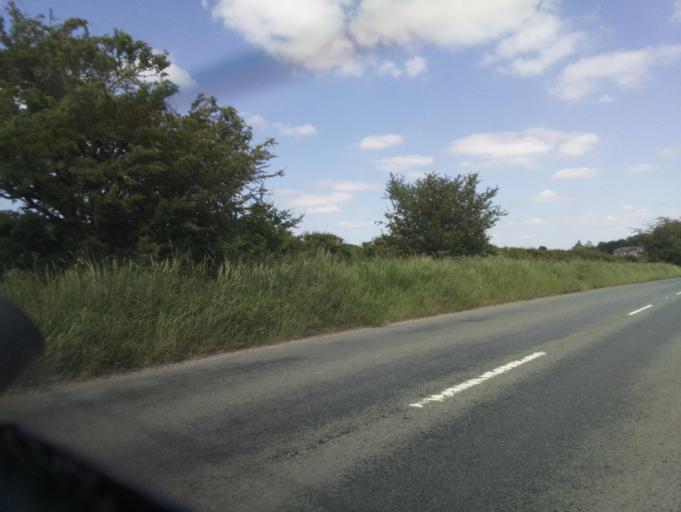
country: GB
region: England
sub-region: Wiltshire
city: Avebury
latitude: 51.4180
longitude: -1.8803
